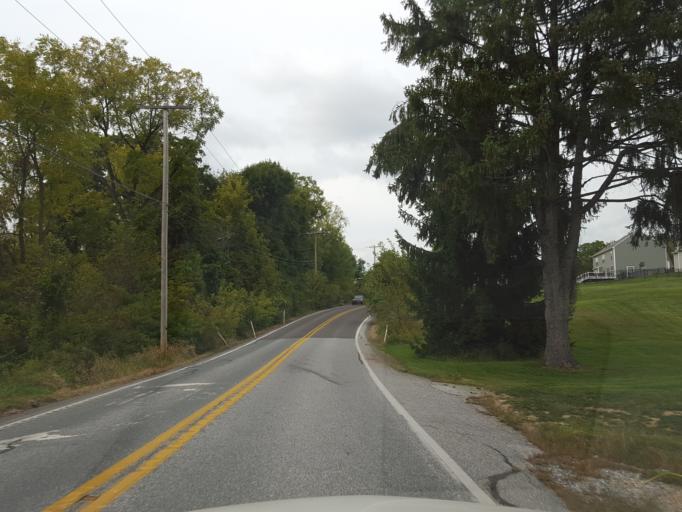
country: US
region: Pennsylvania
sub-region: York County
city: Yoe
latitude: 39.9352
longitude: -76.6539
